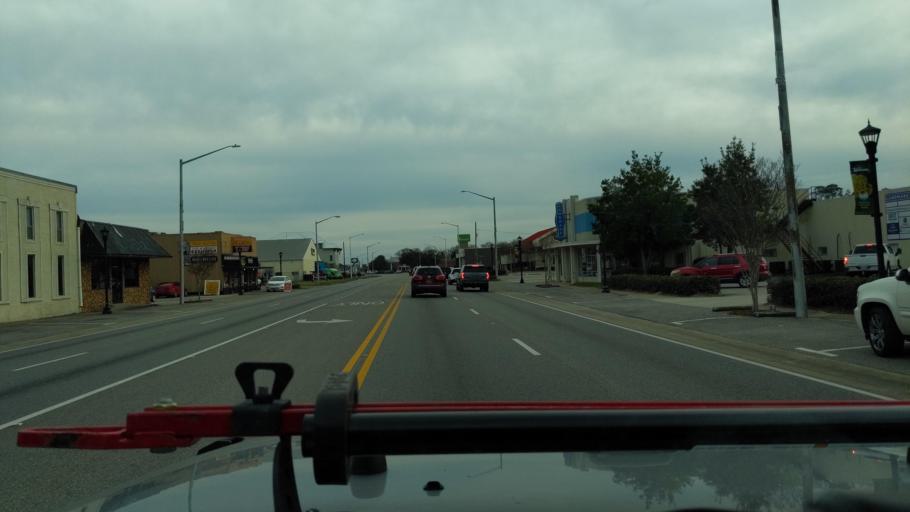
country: US
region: Alabama
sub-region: Baldwin County
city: Foley
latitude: 30.4040
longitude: -87.6838
